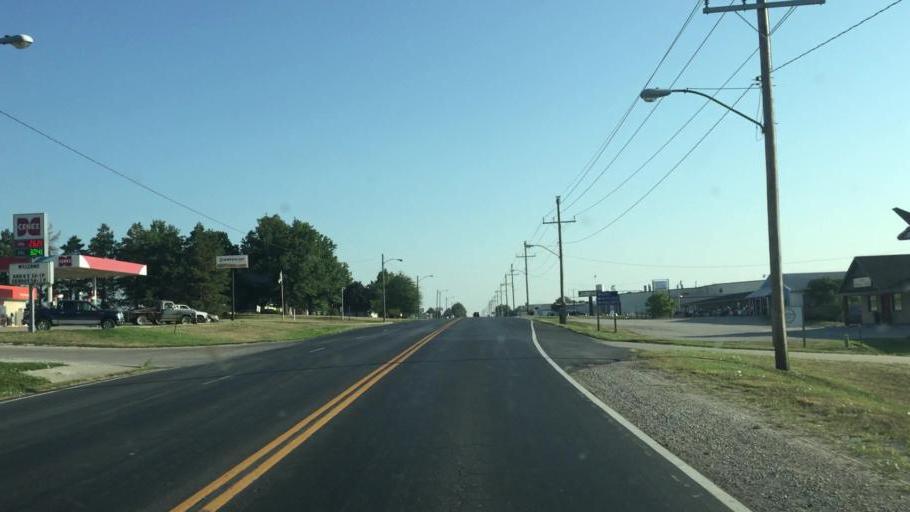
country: US
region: Kansas
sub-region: Nemaha County
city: Sabetha
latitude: 39.8935
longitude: -95.7883
